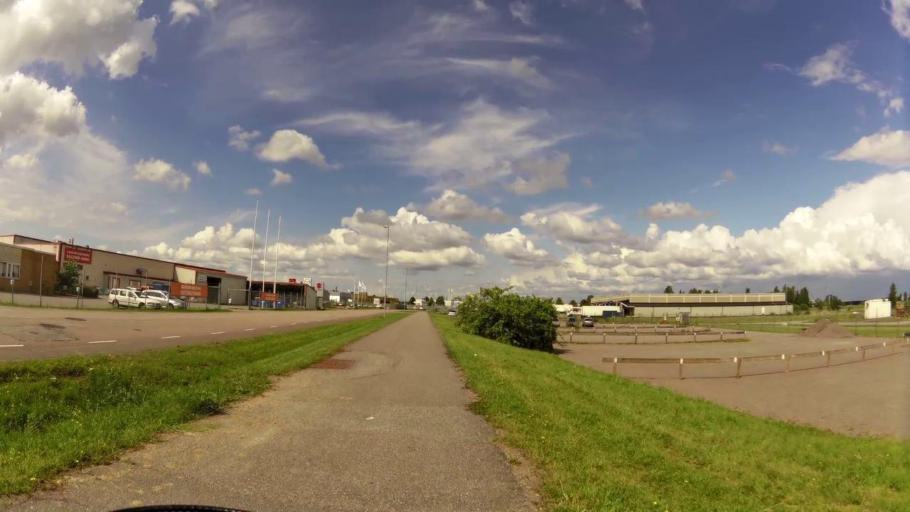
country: SE
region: OEstergoetland
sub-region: Linkopings Kommun
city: Linkoping
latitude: 58.4253
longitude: 15.5953
